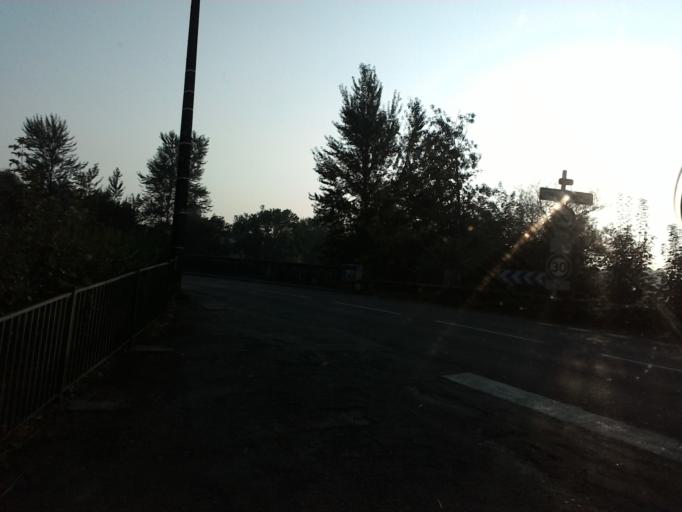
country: FR
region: Franche-Comte
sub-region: Departement du Doubs
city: Devecey
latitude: 47.3370
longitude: 6.0167
